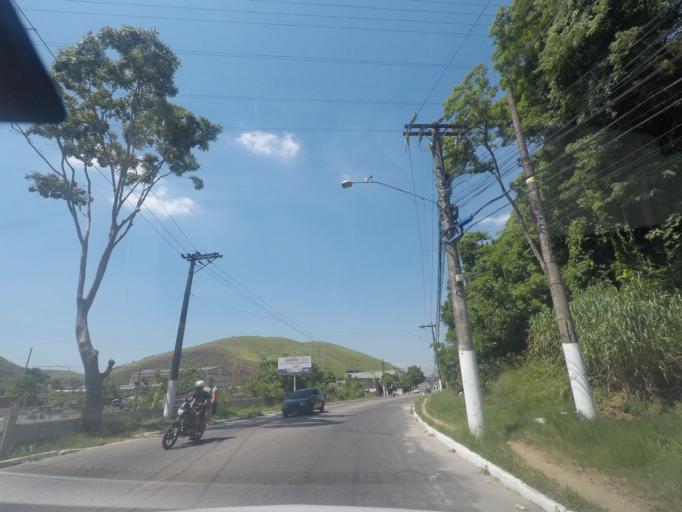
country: BR
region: Rio de Janeiro
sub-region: Petropolis
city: Petropolis
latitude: -22.5999
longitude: -43.1875
